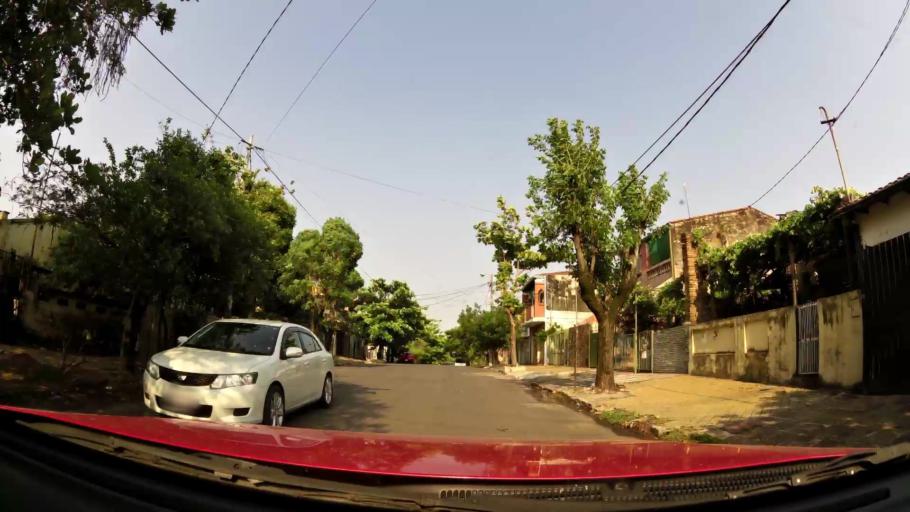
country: PY
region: Presidente Hayes
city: Nanawa
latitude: -25.2810
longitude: -57.6601
